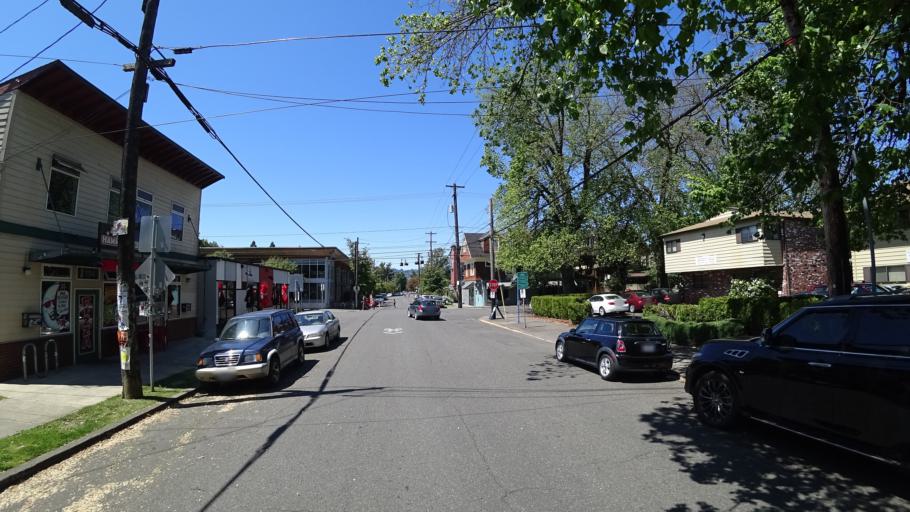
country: US
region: Oregon
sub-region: Multnomah County
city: Portland
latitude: 45.5034
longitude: -122.6442
